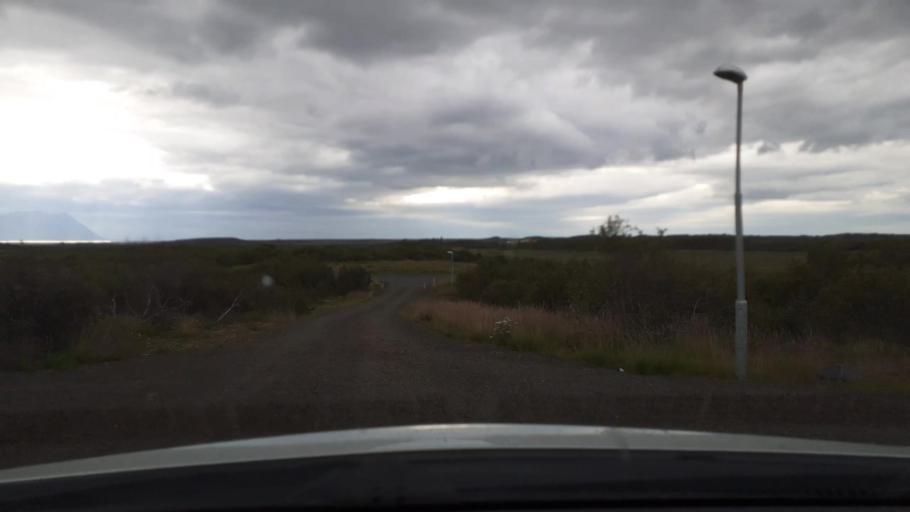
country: IS
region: West
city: Borgarnes
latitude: 64.6769
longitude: -21.7072
